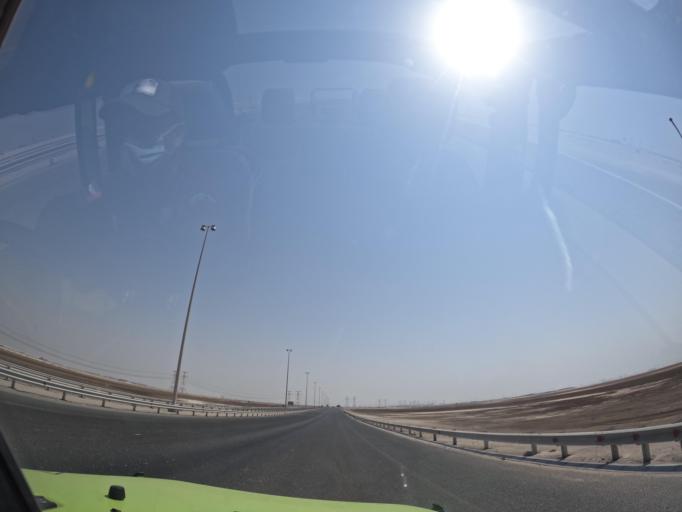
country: AE
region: Abu Dhabi
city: Abu Dhabi
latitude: 24.2101
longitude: 54.4163
